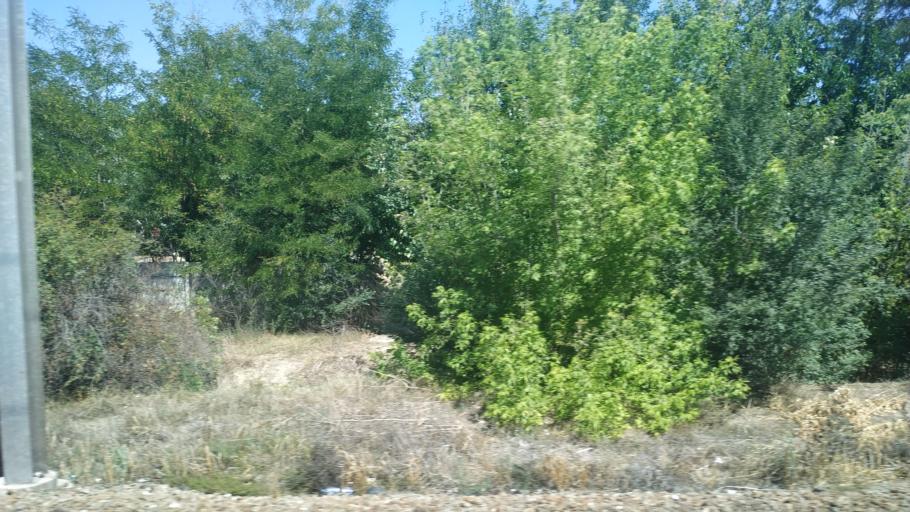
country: RO
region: Constanta
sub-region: Oras Murfatlar
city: Murfatlar
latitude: 44.1739
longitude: 28.4057
